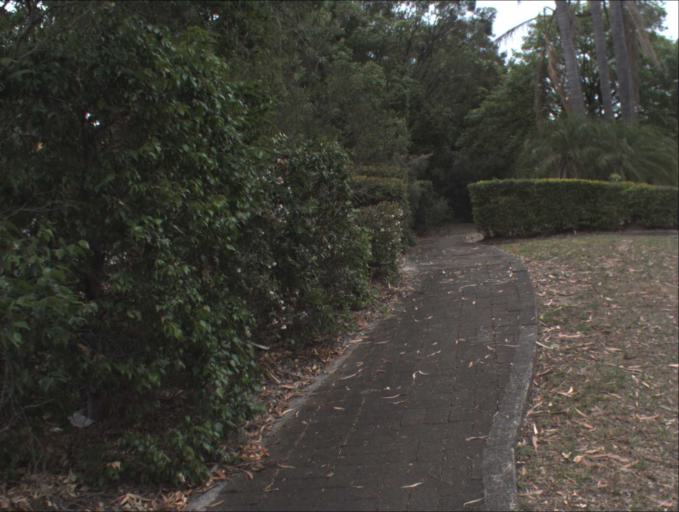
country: AU
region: Queensland
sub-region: Logan
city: Springwood
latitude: -27.6134
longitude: 153.1241
